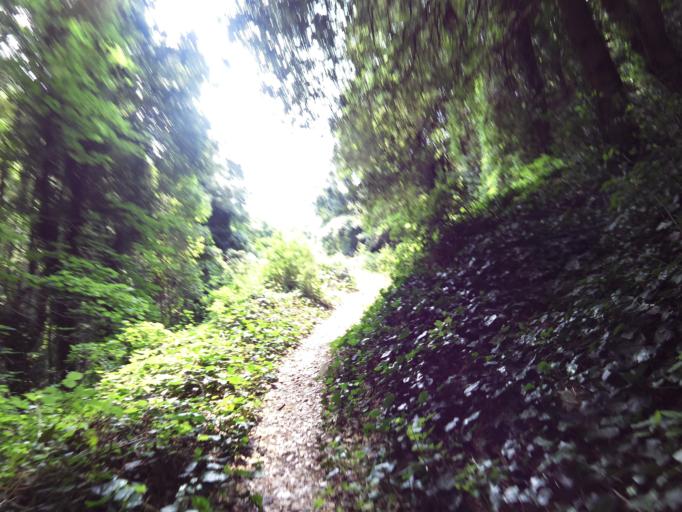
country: IT
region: Calabria
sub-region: Provincia di Reggio Calabria
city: Bivongi
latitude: 38.5012
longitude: 16.3984
